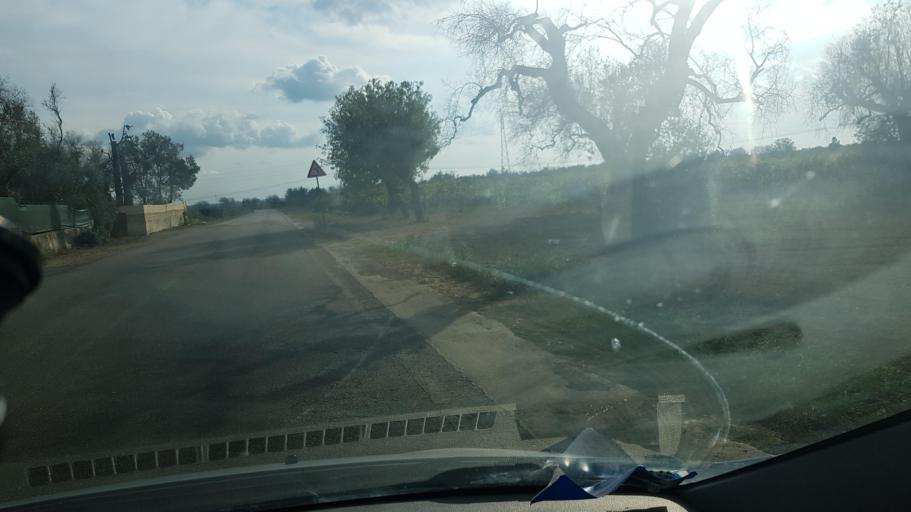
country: IT
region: Apulia
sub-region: Provincia di Brindisi
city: Cellino San Marco
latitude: 40.4599
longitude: 17.9570
